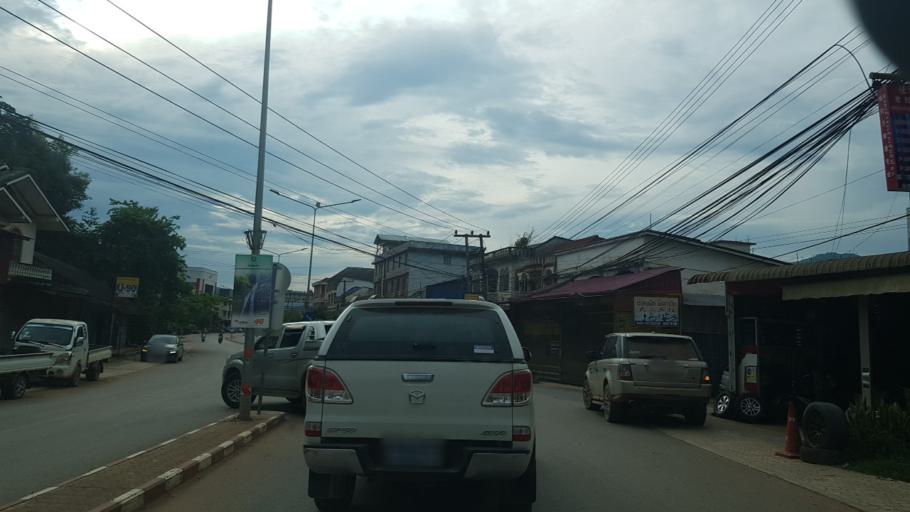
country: LA
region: Oudomxai
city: Muang Xay
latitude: 20.6881
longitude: 101.9865
